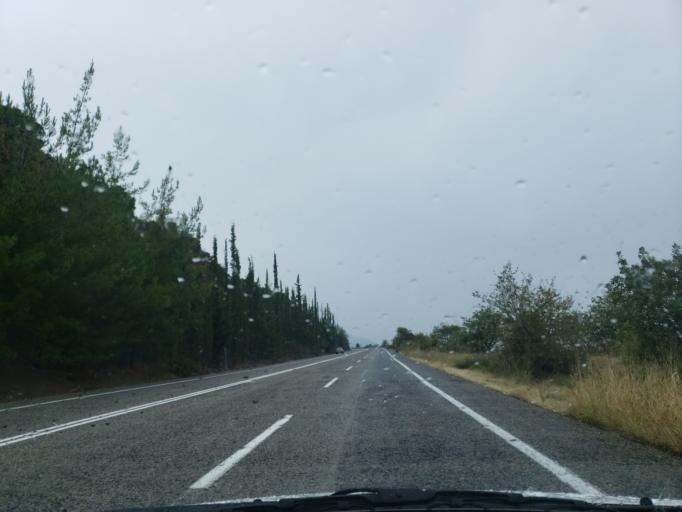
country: GR
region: Central Greece
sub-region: Nomos Fthiotidos
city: Anthili
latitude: 38.7932
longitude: 22.4798
